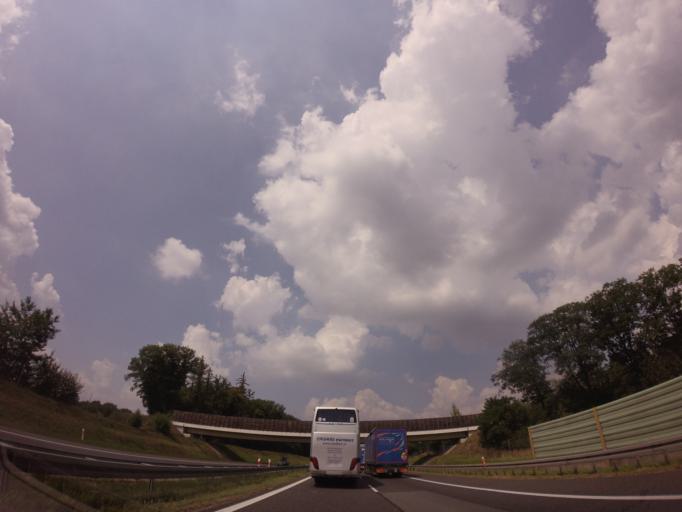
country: PL
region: Silesian Voivodeship
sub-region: Powiat gliwicki
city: Rudziniec
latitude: 50.3828
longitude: 18.4626
